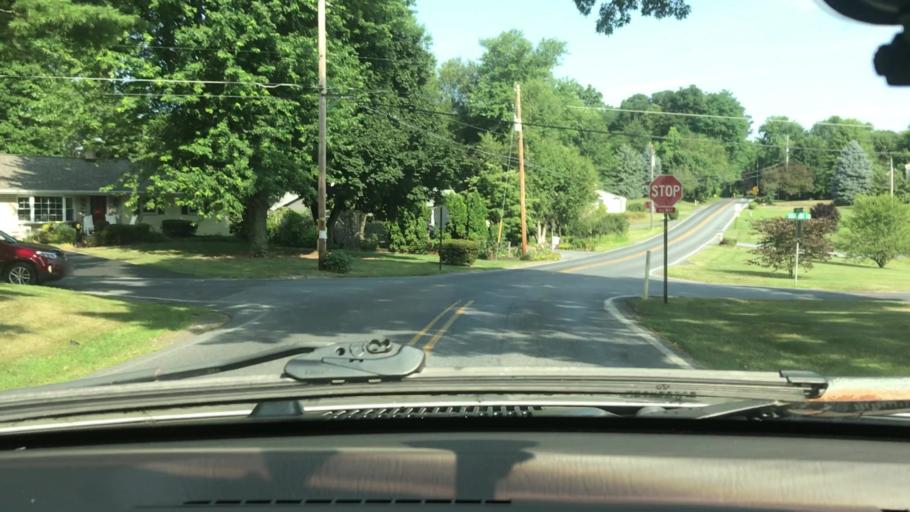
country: US
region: Pennsylvania
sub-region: Lancaster County
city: Rheems
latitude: 40.1444
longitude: -76.5720
